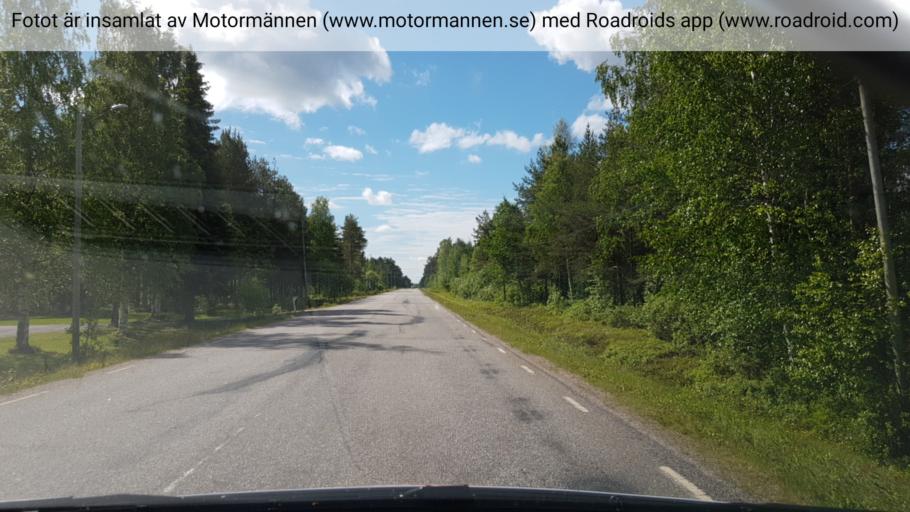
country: FI
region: Lapland
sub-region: Torniolaakso
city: Pello
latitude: 66.7967
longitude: 23.8955
